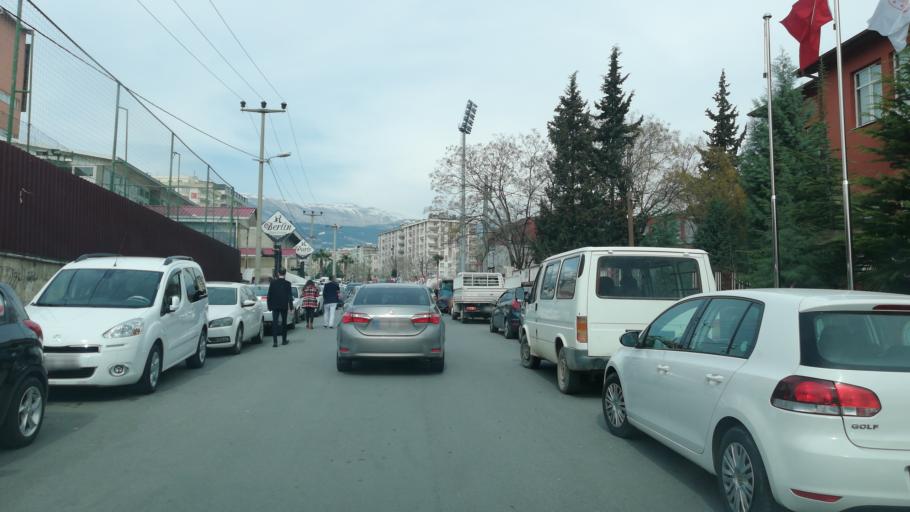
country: TR
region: Kahramanmaras
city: Kahramanmaras
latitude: 37.5736
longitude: 36.9219
